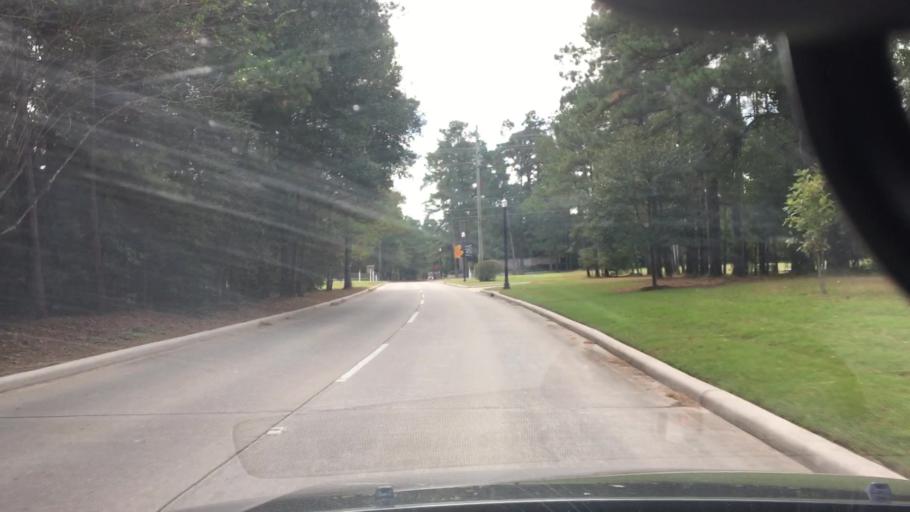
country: US
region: Texas
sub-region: Harris County
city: Humble
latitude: 29.9359
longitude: -95.2689
